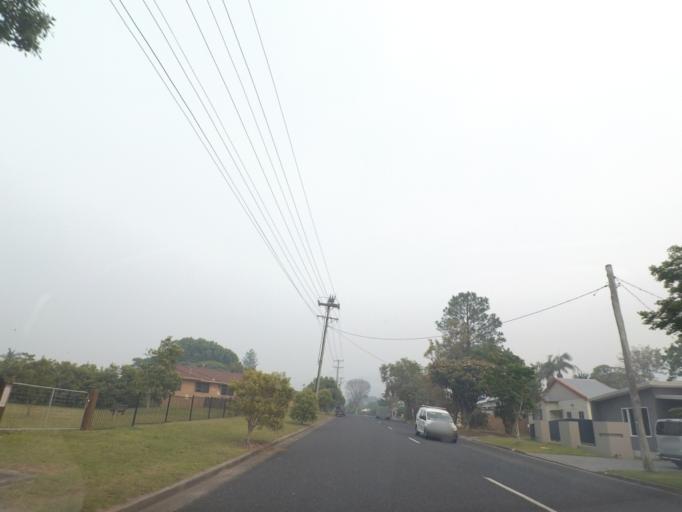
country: AU
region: New South Wales
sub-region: Coffs Harbour
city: Coffs Harbour
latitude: -30.2865
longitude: 153.1072
